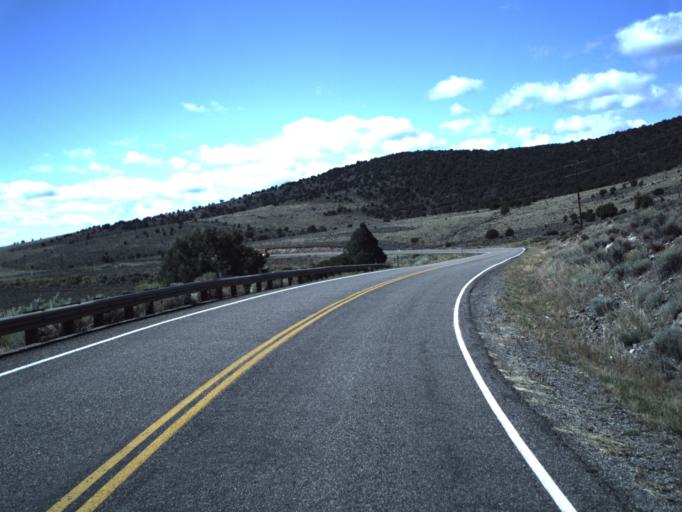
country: US
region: Utah
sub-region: Sevier County
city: Monroe
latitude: 38.5492
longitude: -111.8672
